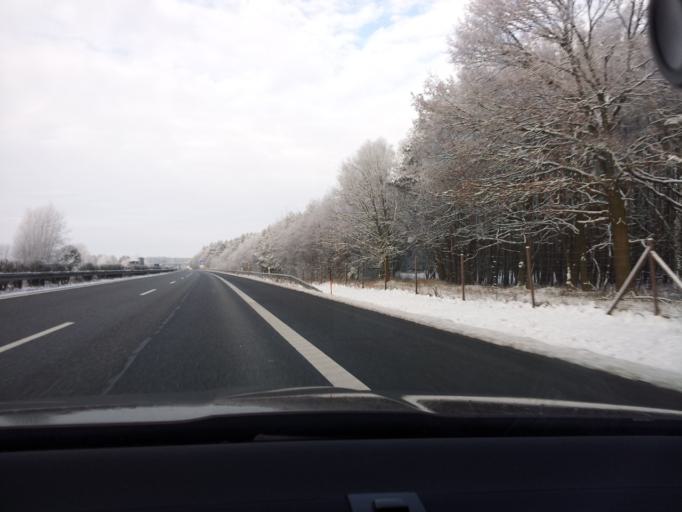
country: DE
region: Mecklenburg-Vorpommern
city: Spornitz
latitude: 53.3604
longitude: 11.7570
